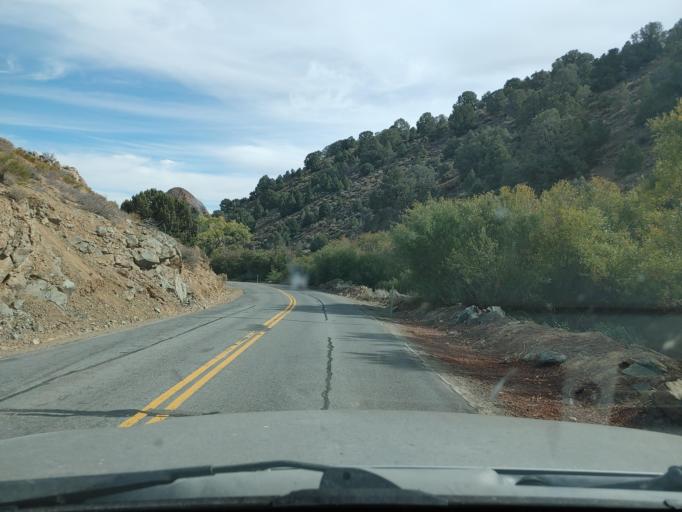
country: US
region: Nevada
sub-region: Storey County
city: Virginia City
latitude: 39.3063
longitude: -119.6276
